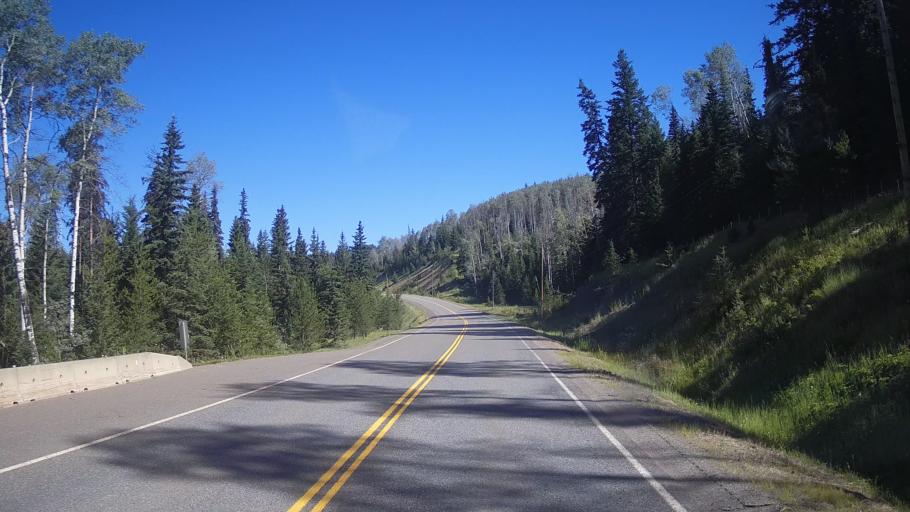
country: CA
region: British Columbia
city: Kamloops
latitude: 51.4803
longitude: -120.5623
